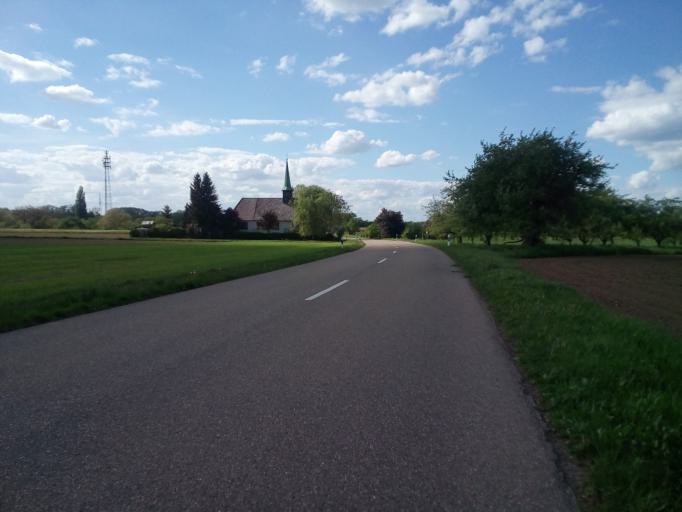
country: DE
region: Baden-Wuerttemberg
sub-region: Karlsruhe Region
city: Lichtenau
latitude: 48.6974
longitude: 7.9834
